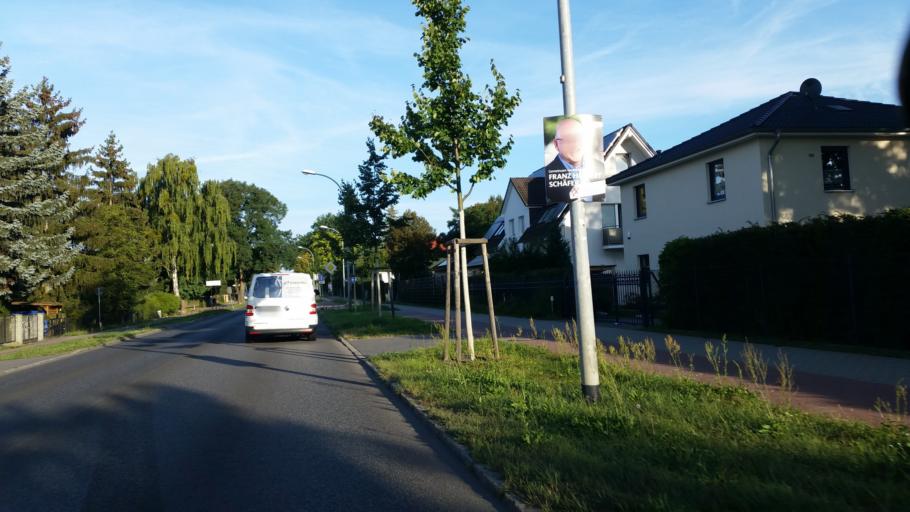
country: DE
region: Brandenburg
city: Teltow
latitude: 52.3933
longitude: 13.2875
